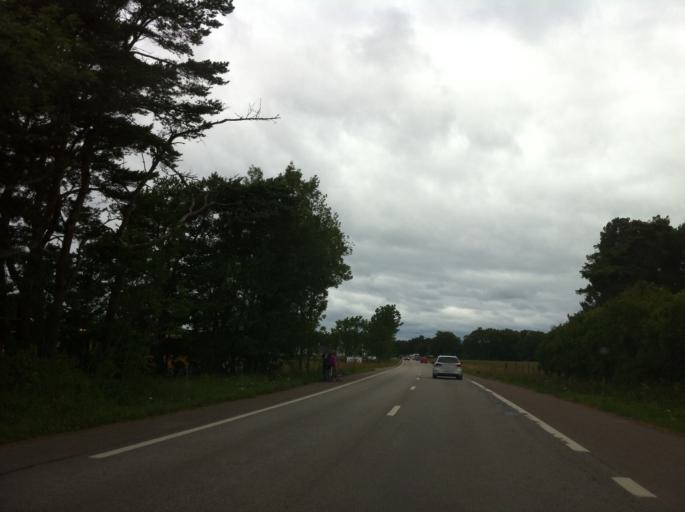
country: SE
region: Kalmar
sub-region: Borgholms Kommun
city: Borgholm
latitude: 57.2486
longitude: 17.0577
